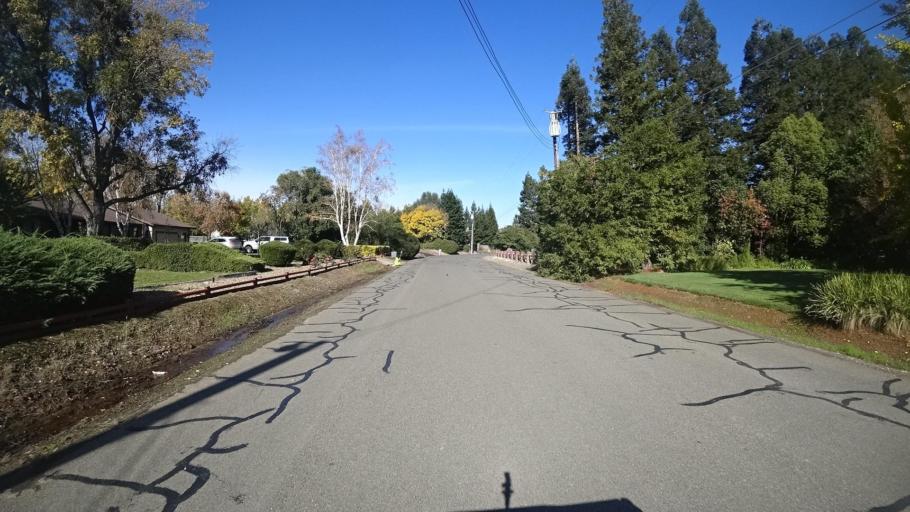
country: US
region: California
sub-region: Sacramento County
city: Vineyard
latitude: 38.4366
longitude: -121.3579
